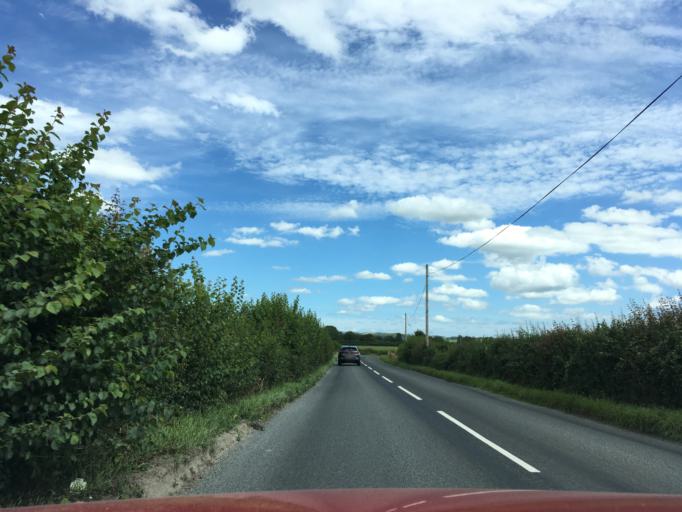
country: GB
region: England
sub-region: Somerset
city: Ilchester
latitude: 51.0461
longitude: -2.6581
